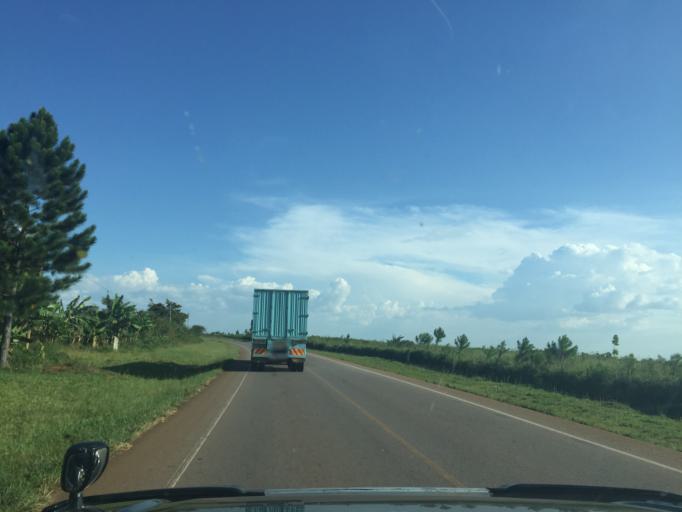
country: UG
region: Central Region
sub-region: Nakasongola District
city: Nakasongola
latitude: 1.2971
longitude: 32.4231
